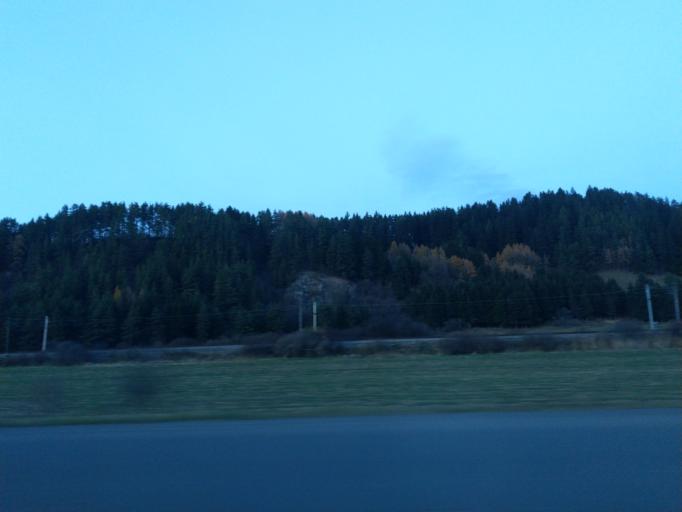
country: SK
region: Zilinsky
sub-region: Okres Zilina
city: Liptovsky Hradok
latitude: 49.0632
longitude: 19.6877
